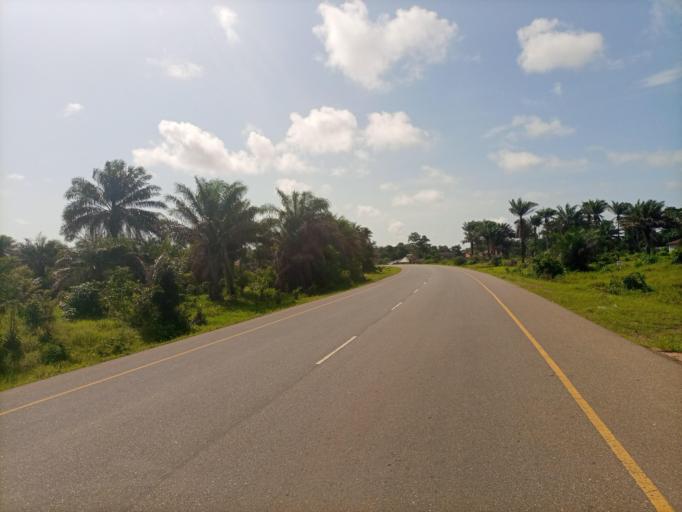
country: SL
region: Northern Province
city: Masoyila
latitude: 8.6219
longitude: -13.1758
